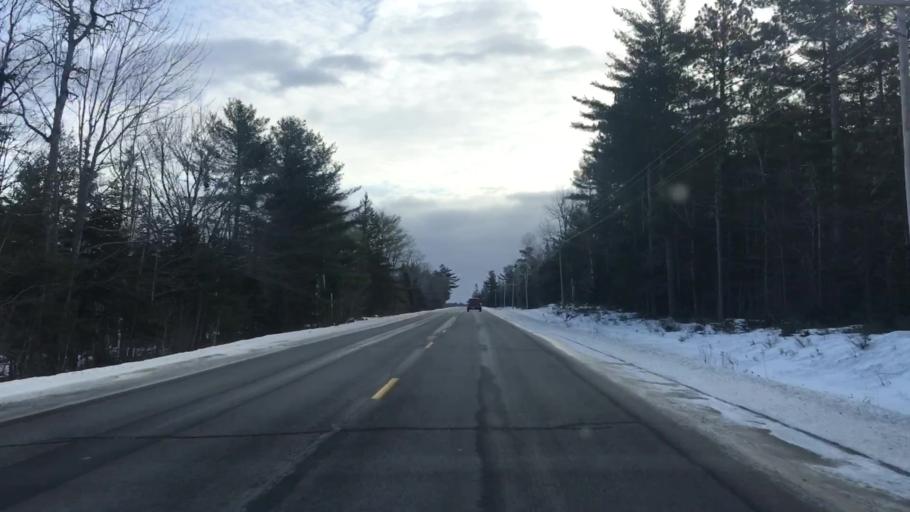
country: US
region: Maine
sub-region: Washington County
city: Machias
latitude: 44.9998
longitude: -67.5977
